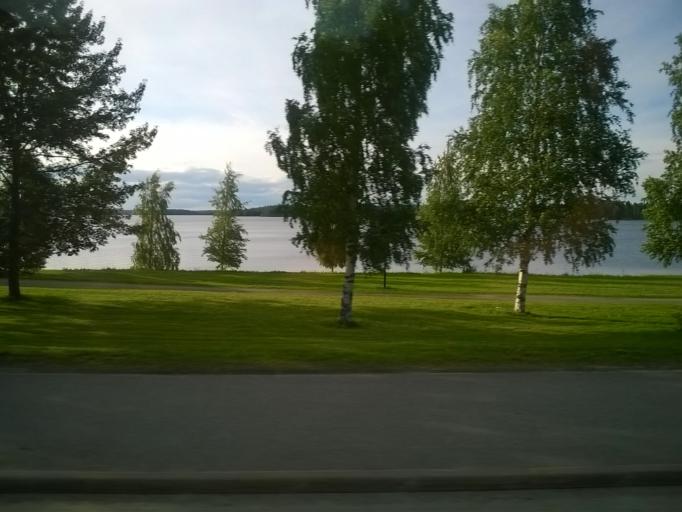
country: FI
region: Kainuu
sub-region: Kajaani
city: Sotkamo
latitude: 64.1296
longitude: 28.3746
